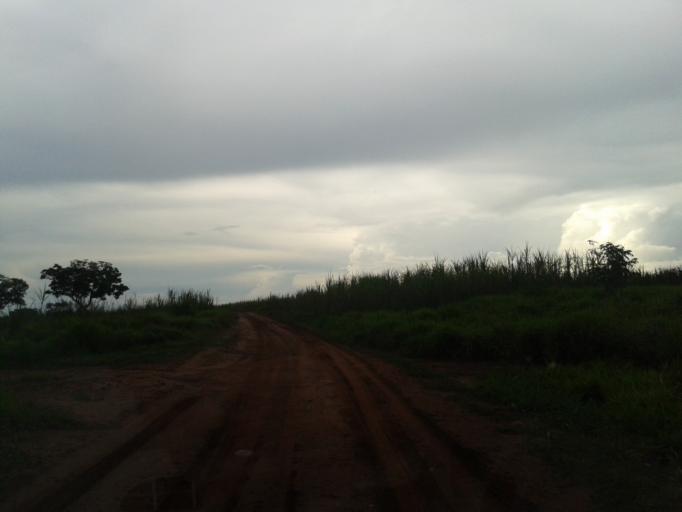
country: BR
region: Minas Gerais
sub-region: Santa Vitoria
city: Santa Vitoria
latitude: -19.1672
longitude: -50.5459
